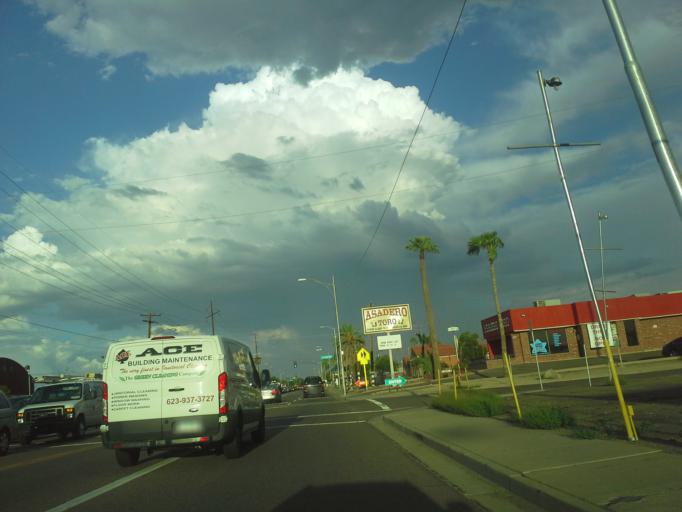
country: US
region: Arizona
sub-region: Maricopa County
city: Phoenix
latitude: 33.4658
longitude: -112.0971
